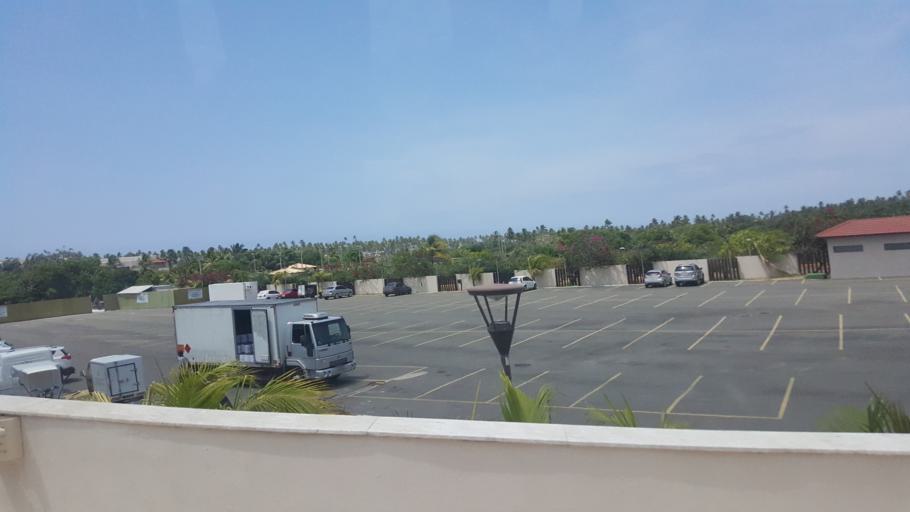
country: BR
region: Bahia
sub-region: Mata De Sao Joao
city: Mata de Sao Joao
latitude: -12.4825
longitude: -37.9569
